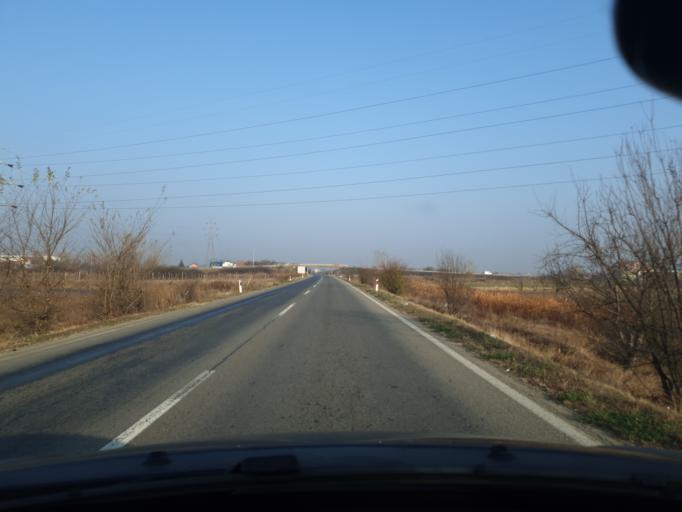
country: RS
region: Central Serbia
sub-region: Jablanicki Okrug
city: Leskovac
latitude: 42.9950
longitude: 21.9709
